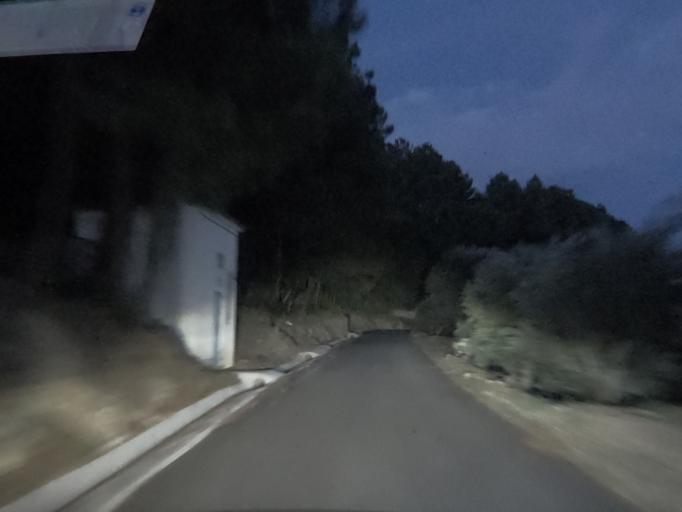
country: PT
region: Vila Real
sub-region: Vila Real
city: Vila Real
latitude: 41.2758
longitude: -7.7582
